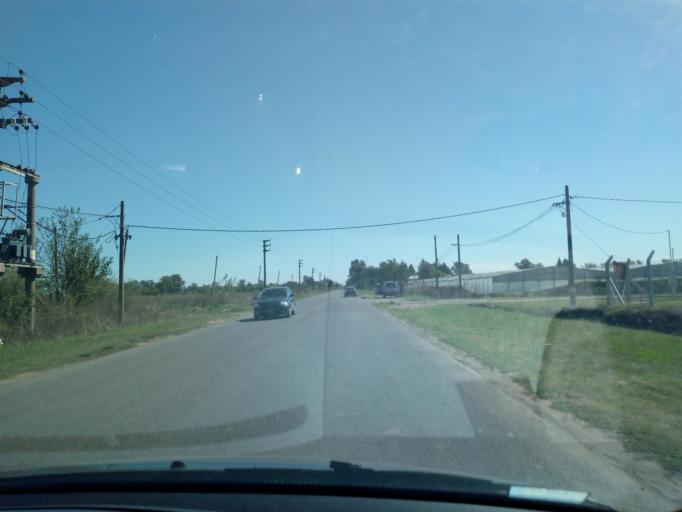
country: AR
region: Buenos Aires
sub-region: Partido de La Plata
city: La Plata
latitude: -35.0058
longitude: -58.0342
